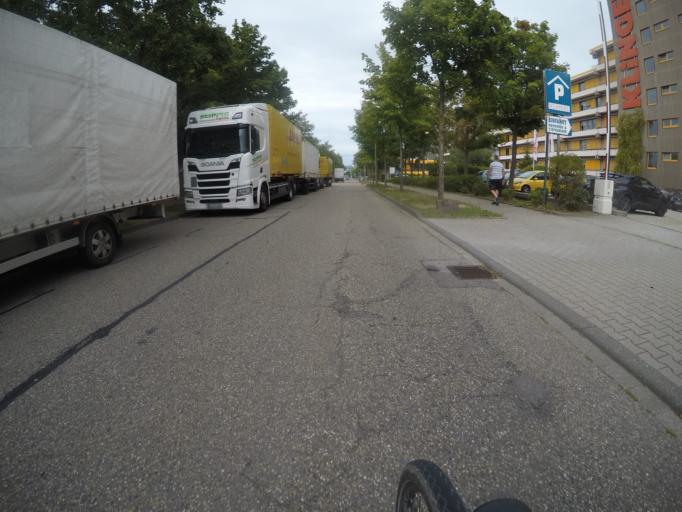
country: DE
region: Baden-Wuerttemberg
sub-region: Karlsruhe Region
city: Eutingen
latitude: 48.8879
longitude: 8.7527
